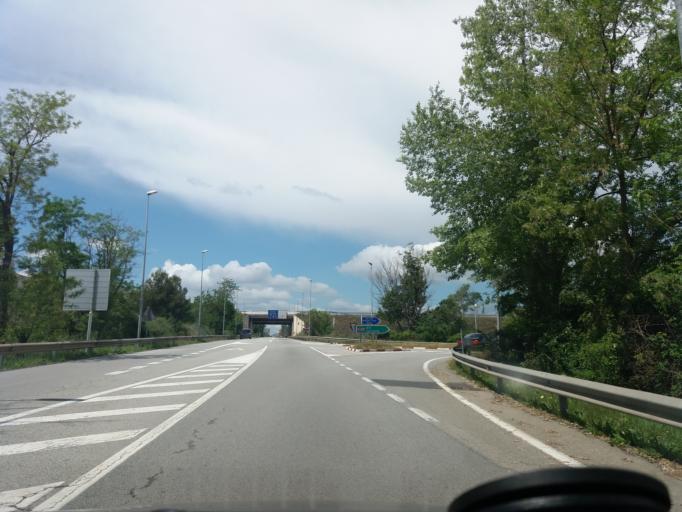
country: ES
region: Catalonia
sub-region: Provincia de Barcelona
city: Navarcles
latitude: 41.7557
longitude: 1.8882
